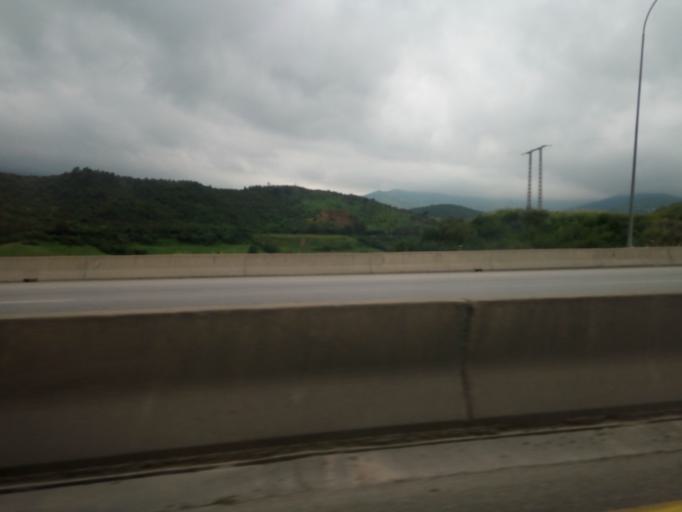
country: DZ
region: Bouira
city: Lakhdaria
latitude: 36.5798
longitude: 3.5474
